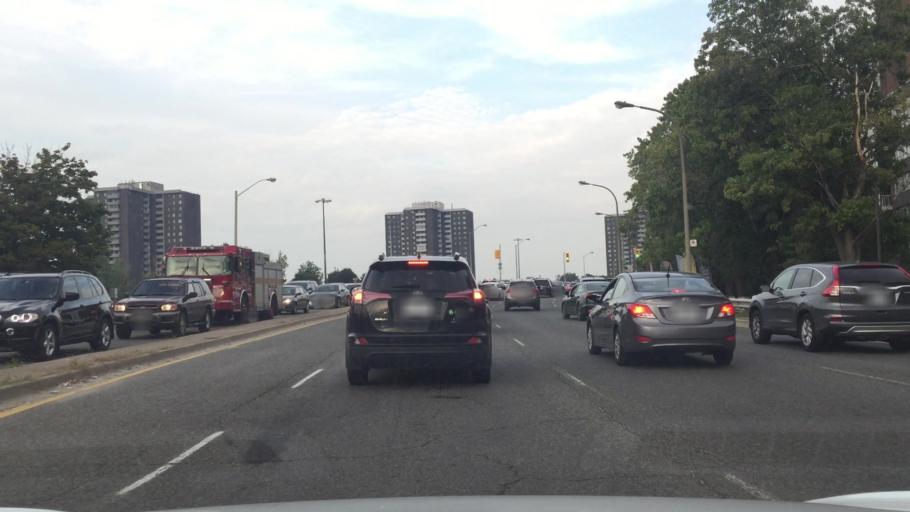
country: CA
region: Ontario
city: Willowdale
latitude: 43.7760
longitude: -79.3428
